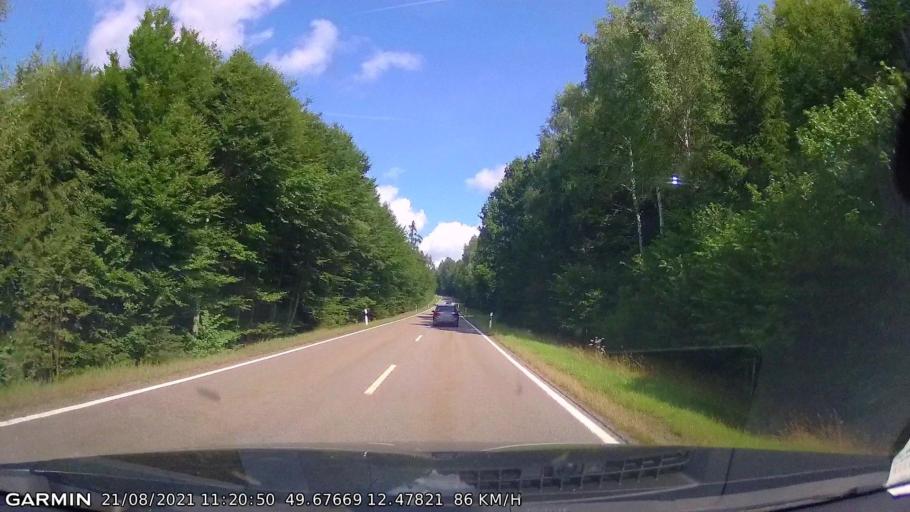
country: DE
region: Bavaria
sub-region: Upper Palatinate
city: Waidhaus
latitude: 49.6769
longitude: 12.4782
